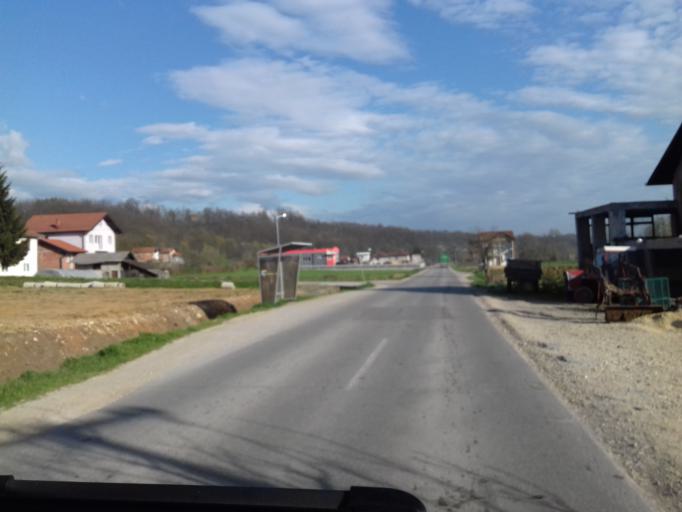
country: BA
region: Federation of Bosnia and Herzegovina
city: Tesanjka
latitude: 44.6477
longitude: 18.0182
